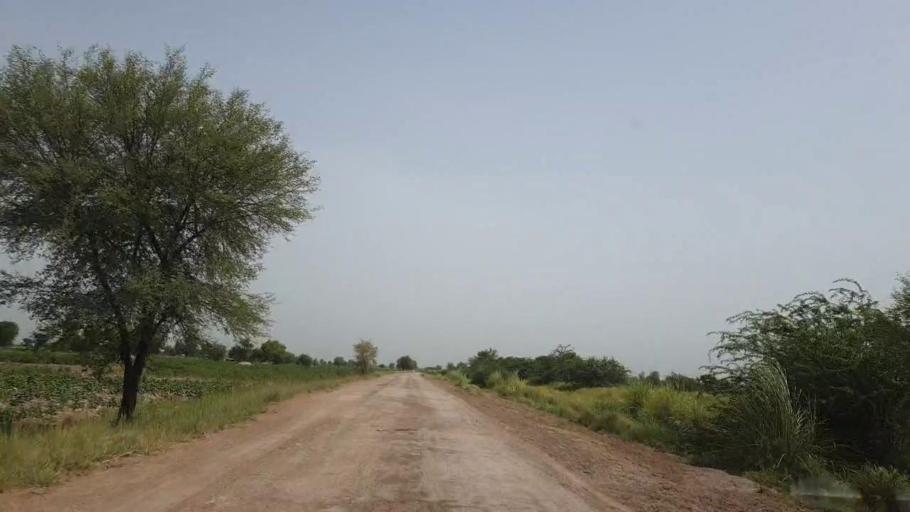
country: PK
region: Sindh
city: Sakrand
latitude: 26.1303
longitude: 68.3642
